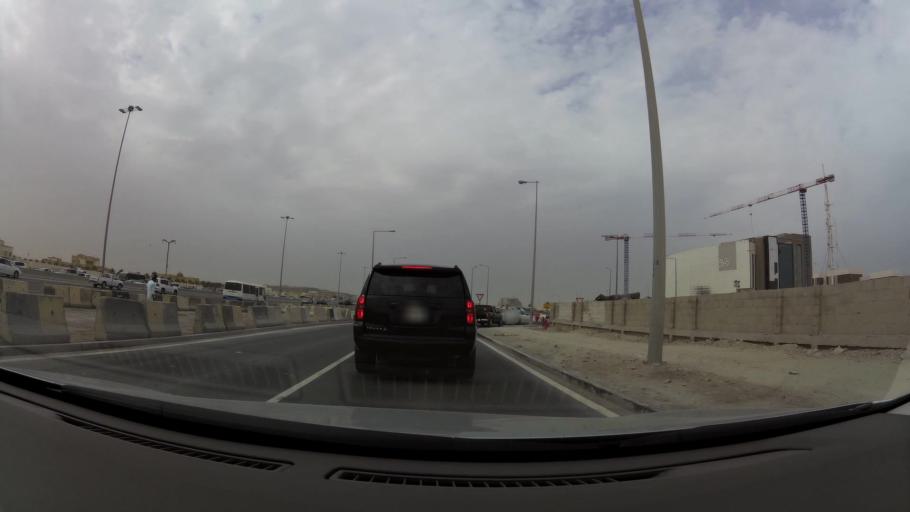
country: QA
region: Baladiyat ar Rayyan
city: Ar Rayyan
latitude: 25.3511
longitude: 51.4552
